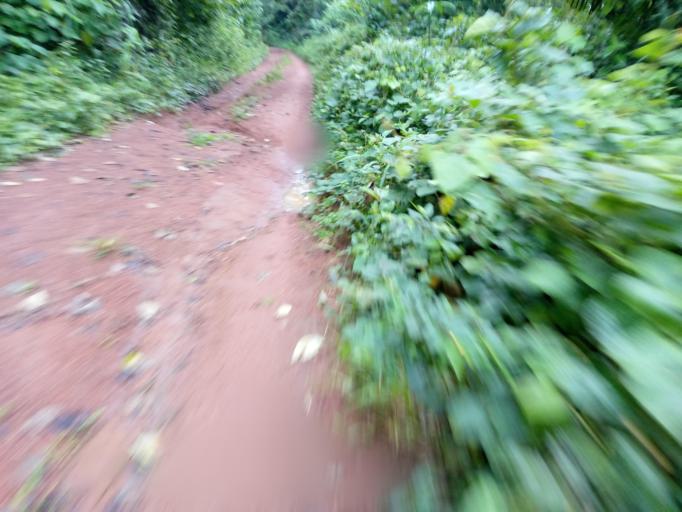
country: SL
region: Eastern Province
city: Buedu
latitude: 8.4699
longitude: -10.3469
